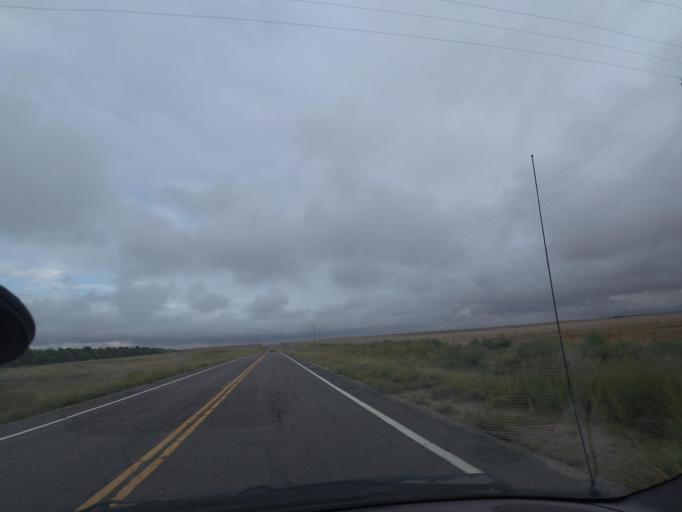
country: US
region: Colorado
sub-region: Washington County
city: Akron
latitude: 39.6993
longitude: -103.0475
